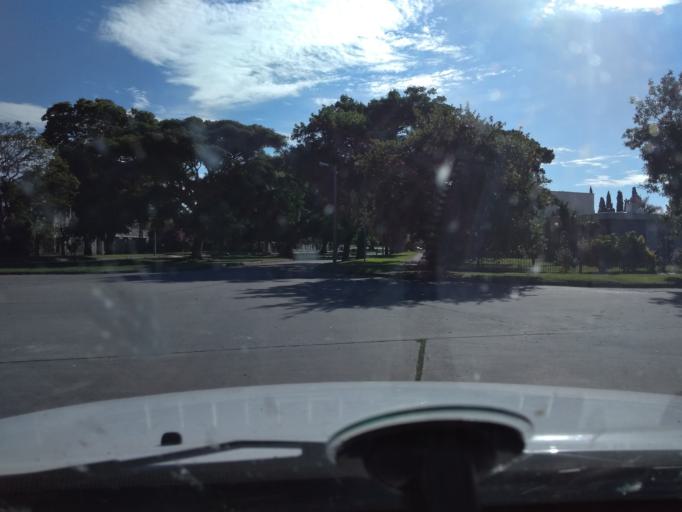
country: UY
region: Canelones
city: Paso de Carrasco
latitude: -34.8886
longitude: -56.0700
